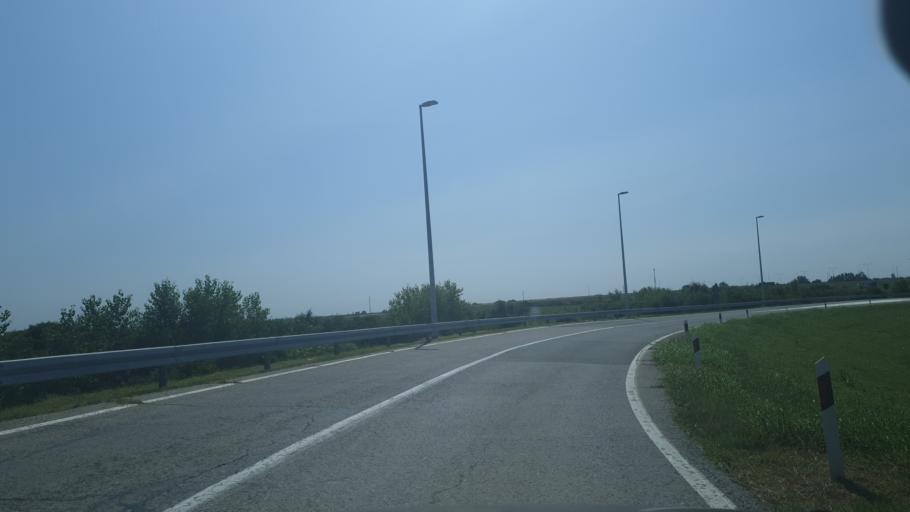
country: RS
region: Autonomna Pokrajina Vojvodina
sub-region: Sremski Okrug
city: Pecinci
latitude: 44.9252
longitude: 19.9533
